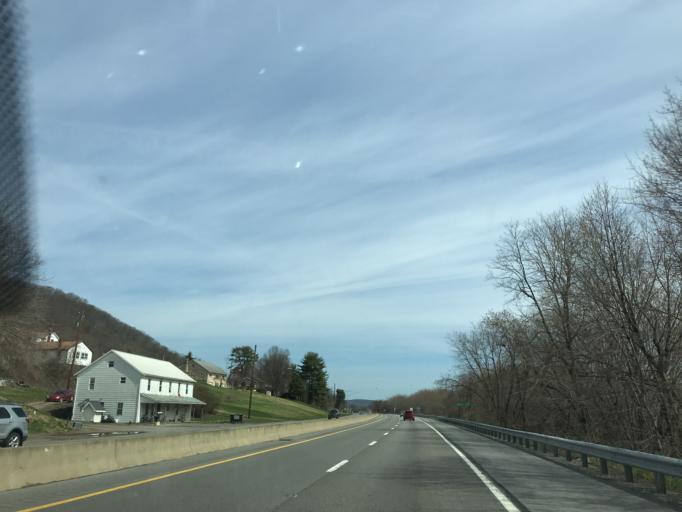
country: US
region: Pennsylvania
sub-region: Snyder County
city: Selinsgrove
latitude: 40.7105
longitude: -76.8621
